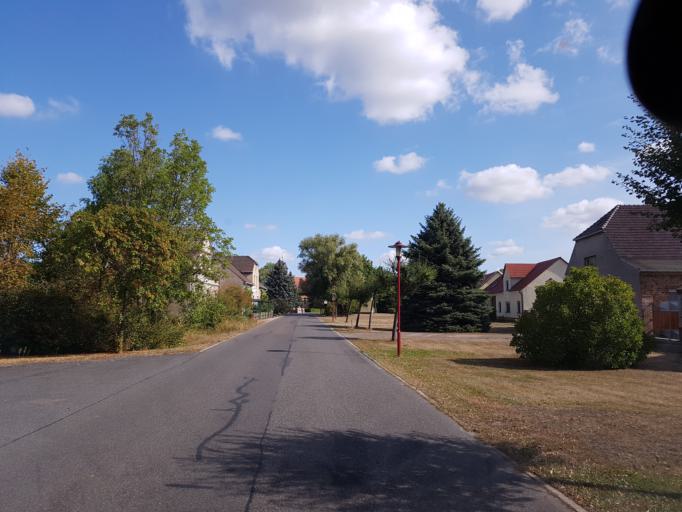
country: DE
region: Brandenburg
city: Sonnewalde
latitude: 51.7324
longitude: 13.6269
